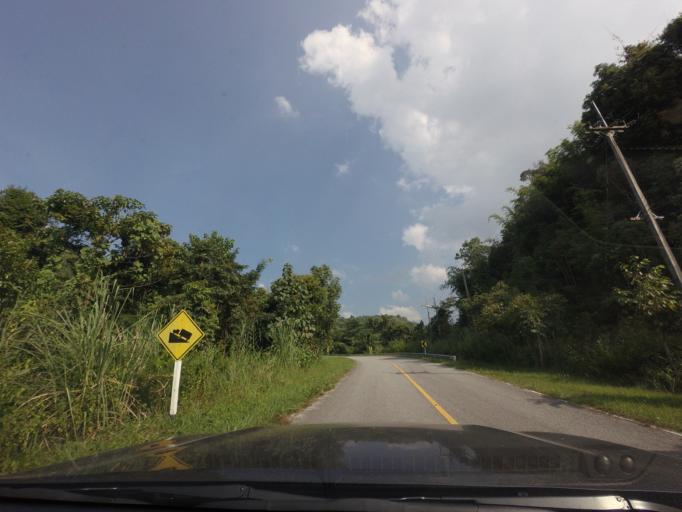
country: TH
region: Phitsanulok
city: Nakhon Thai
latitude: 17.0205
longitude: 100.9719
